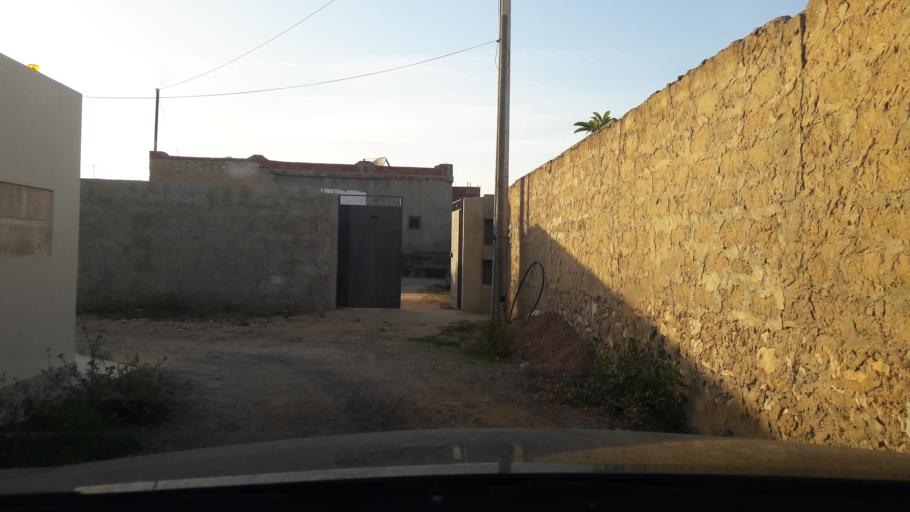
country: TN
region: Safaqis
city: Sfax
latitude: 34.7936
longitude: 10.7500
